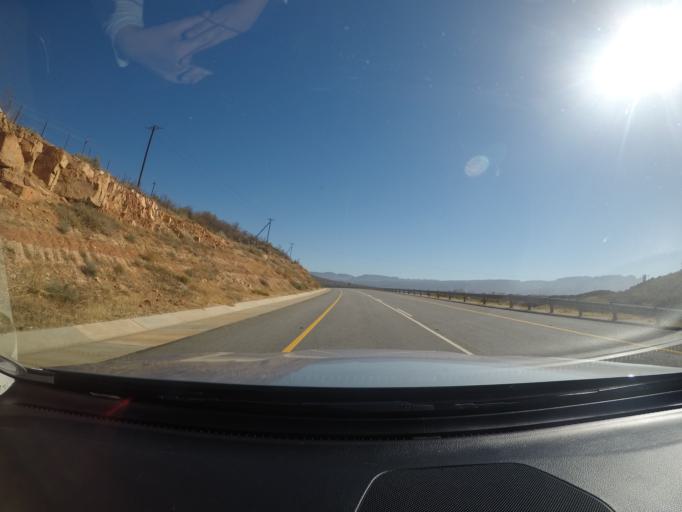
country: ZA
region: Western Cape
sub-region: West Coast District Municipality
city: Clanwilliam
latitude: -32.2164
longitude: 18.8563
